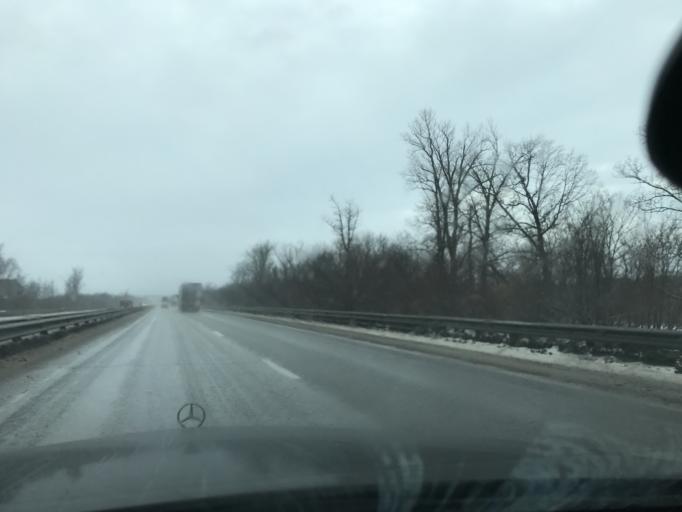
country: RU
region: Vladimir
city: Gorokhovets
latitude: 56.2141
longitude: 42.7527
